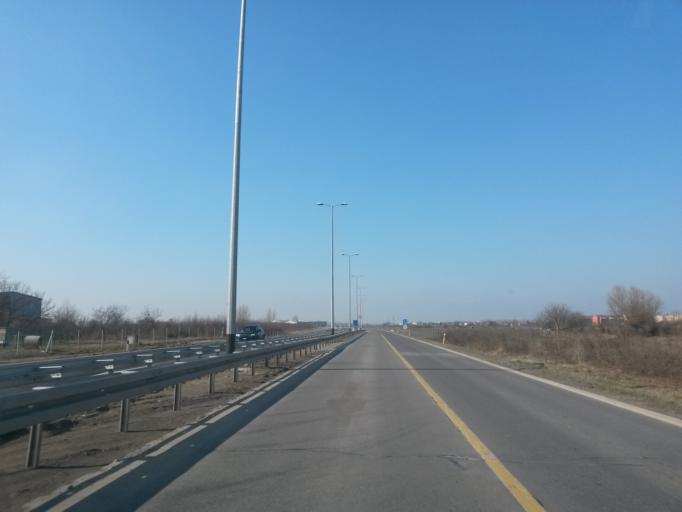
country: HR
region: Osjecko-Baranjska
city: Brijest
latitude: 45.5486
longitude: 18.6588
